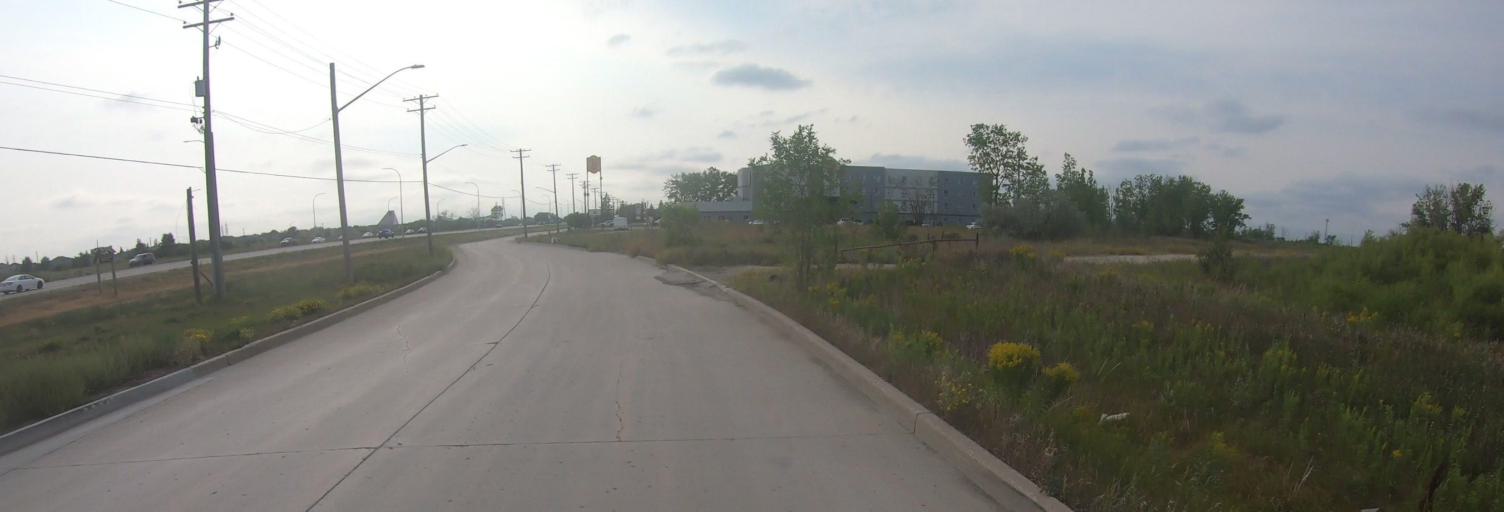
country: CA
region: Manitoba
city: Winnipeg
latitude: 49.8565
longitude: -97.0387
